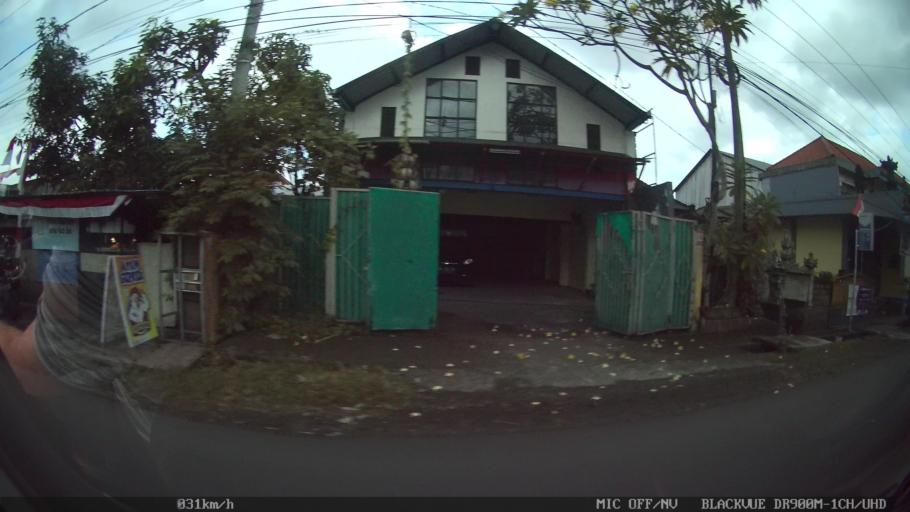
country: ID
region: Bali
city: Banjar Tegal Belodan
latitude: -8.5461
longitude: 115.1203
